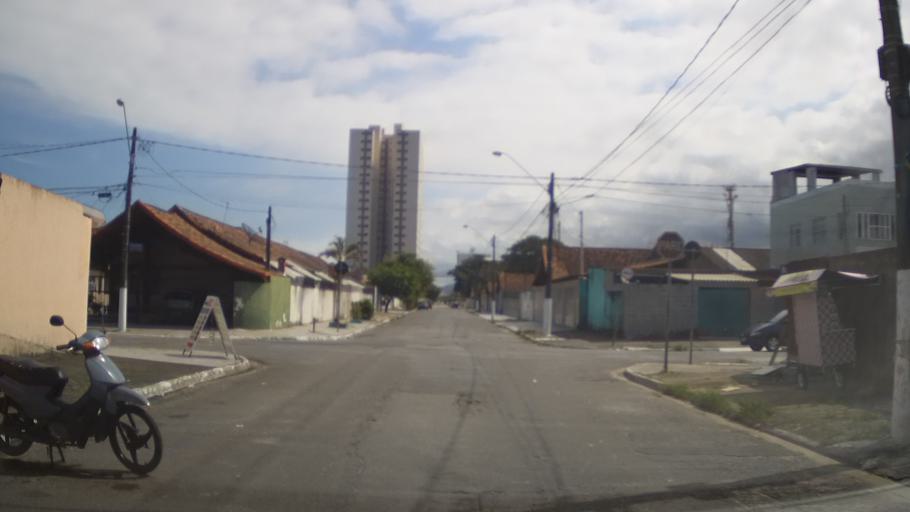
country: BR
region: Sao Paulo
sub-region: Praia Grande
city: Praia Grande
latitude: -24.0147
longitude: -46.4524
